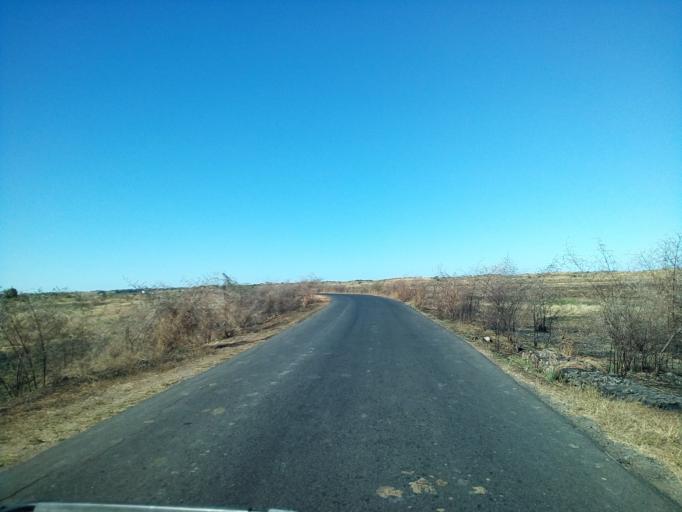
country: MG
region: Boeny
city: Marovoay
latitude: -16.0102
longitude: 46.7013
